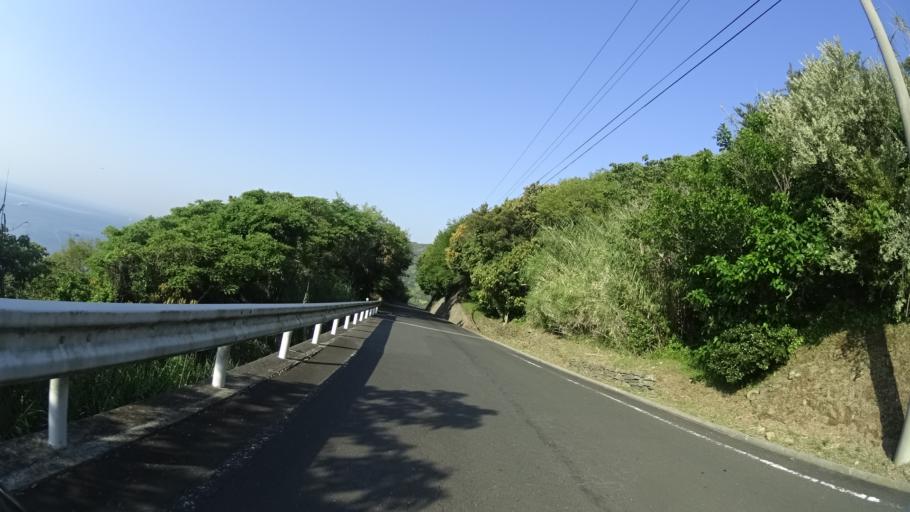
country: JP
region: Ehime
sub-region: Nishiuwa-gun
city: Ikata-cho
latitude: 33.3697
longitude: 132.0532
